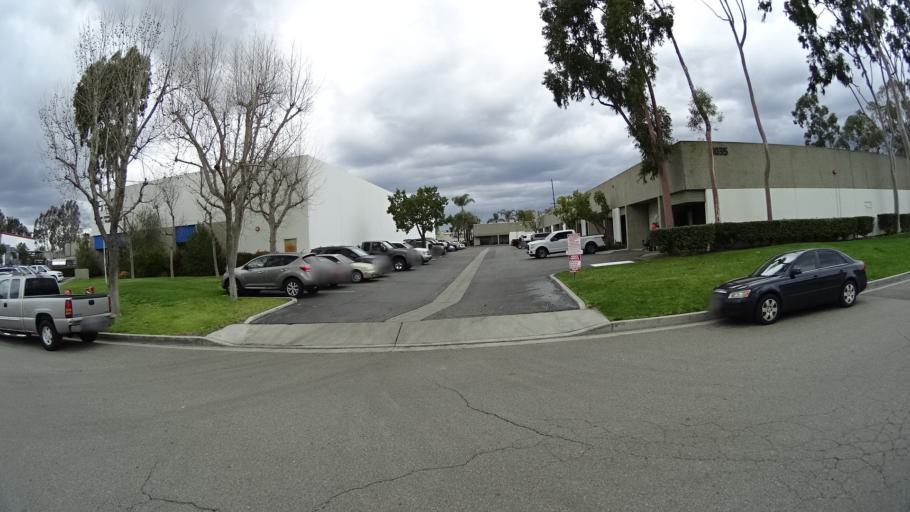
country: US
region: California
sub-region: Orange County
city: Placentia
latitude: 33.8484
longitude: -117.8613
